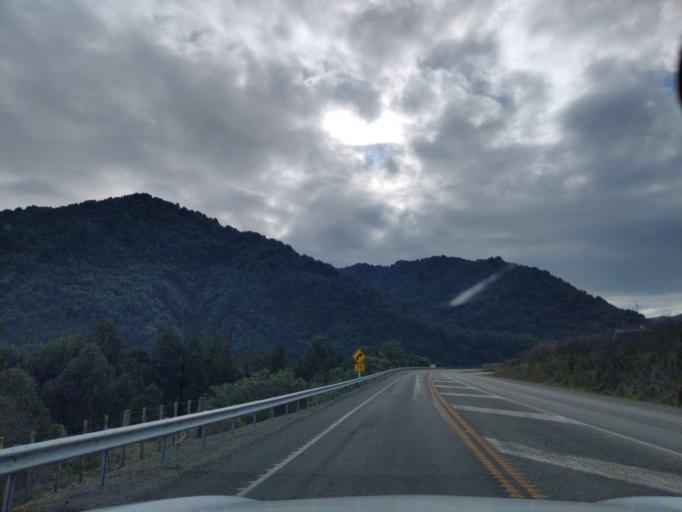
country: NZ
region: Manawatu-Wanganui
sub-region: Palmerston North City
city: Palmerston North
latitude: -40.3363
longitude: 175.8182
